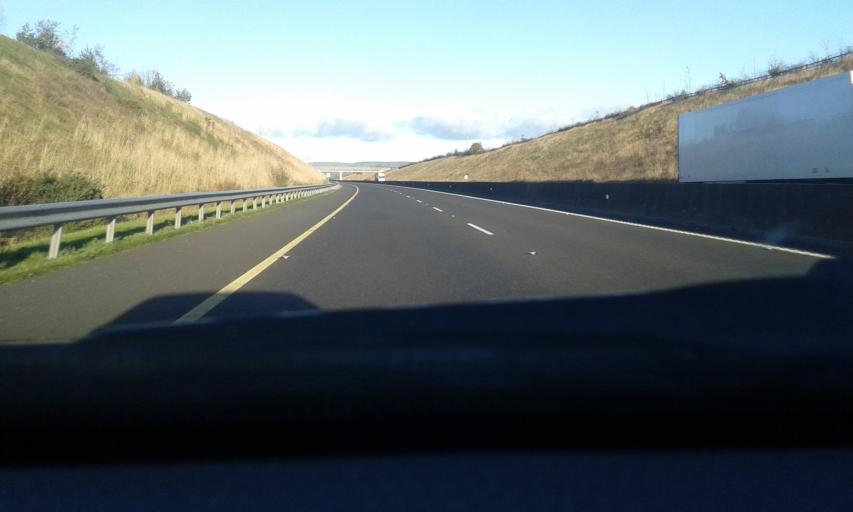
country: IE
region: Leinster
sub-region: Laois
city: Rathdowney
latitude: 52.7109
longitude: -7.6187
